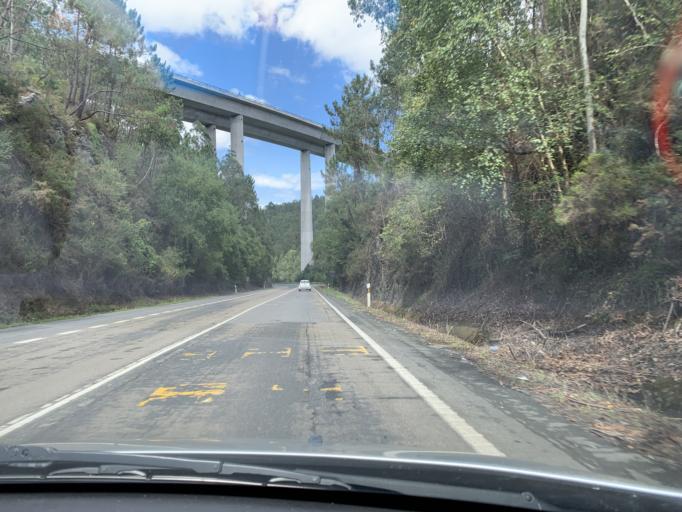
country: ES
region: Galicia
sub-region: Provincia de Lugo
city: Barreiros
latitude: 43.5036
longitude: -7.2712
